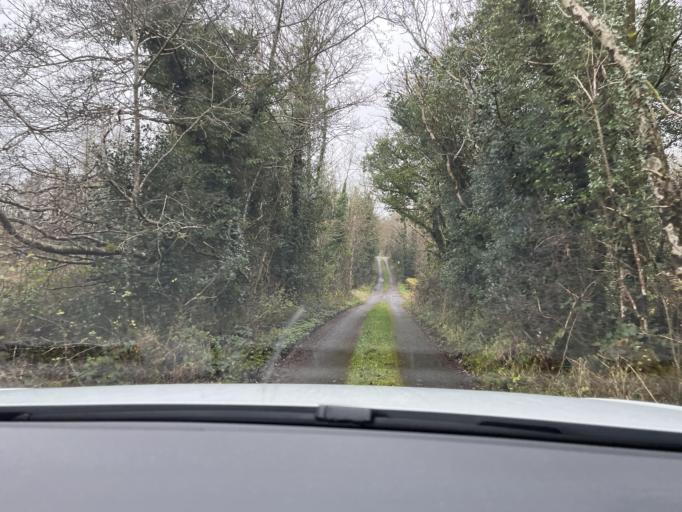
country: IE
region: Connaught
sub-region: County Leitrim
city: Manorhamilton
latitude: 54.2843
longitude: -8.1150
